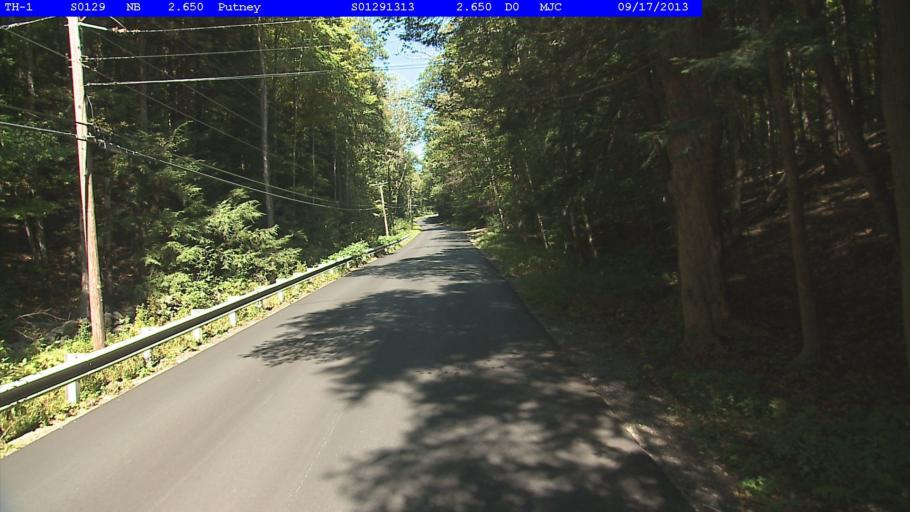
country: US
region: New Hampshire
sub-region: Cheshire County
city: Westmoreland
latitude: 43.0103
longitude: -72.5292
